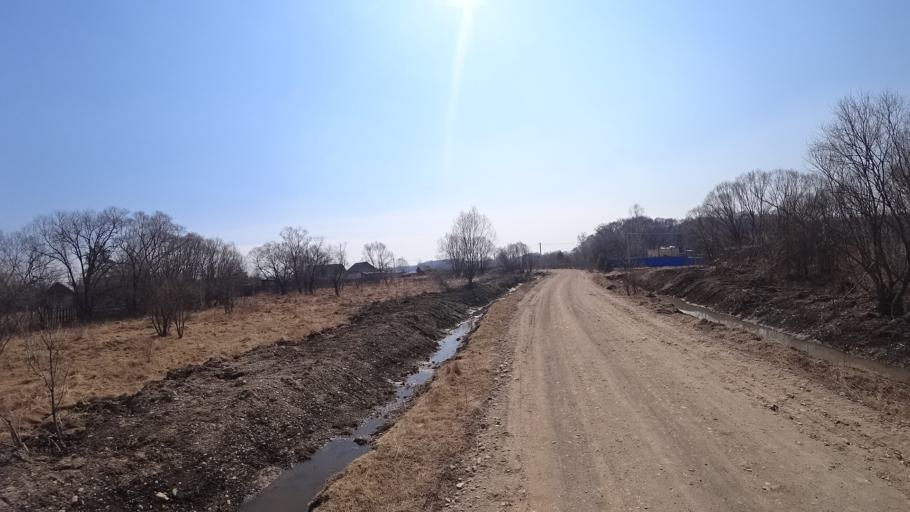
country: RU
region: Amur
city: Novobureyskiy
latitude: 49.7771
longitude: 129.8487
